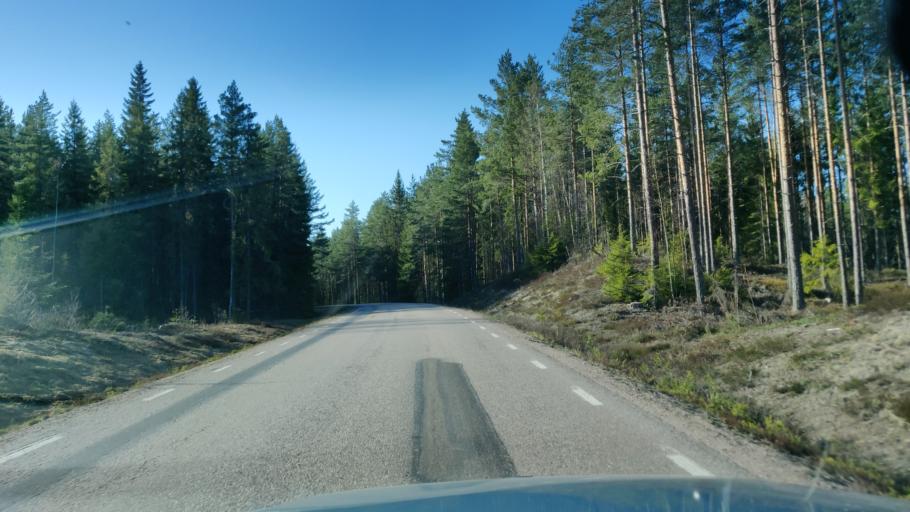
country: SE
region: Vaermland
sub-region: Sunne Kommun
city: Sunne
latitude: 59.9910
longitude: 13.3089
